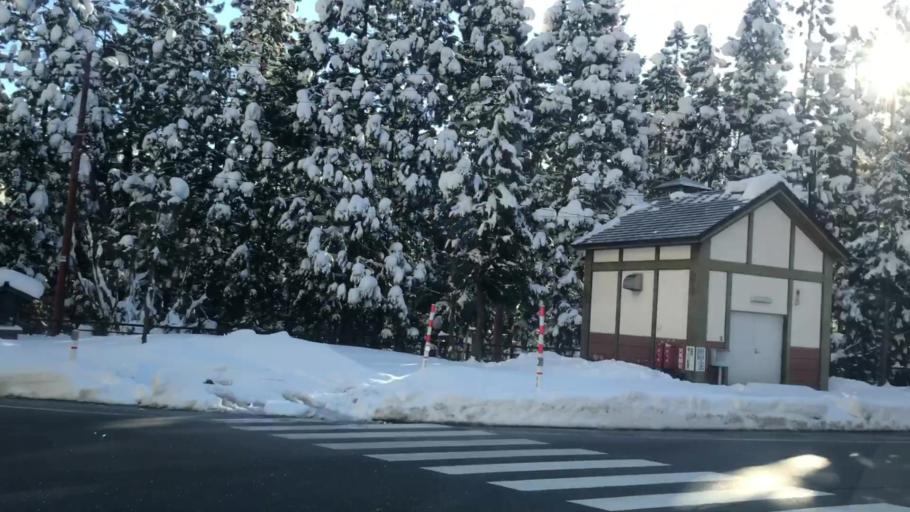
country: JP
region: Toyama
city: Kamiichi
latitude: 36.5830
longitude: 137.4060
